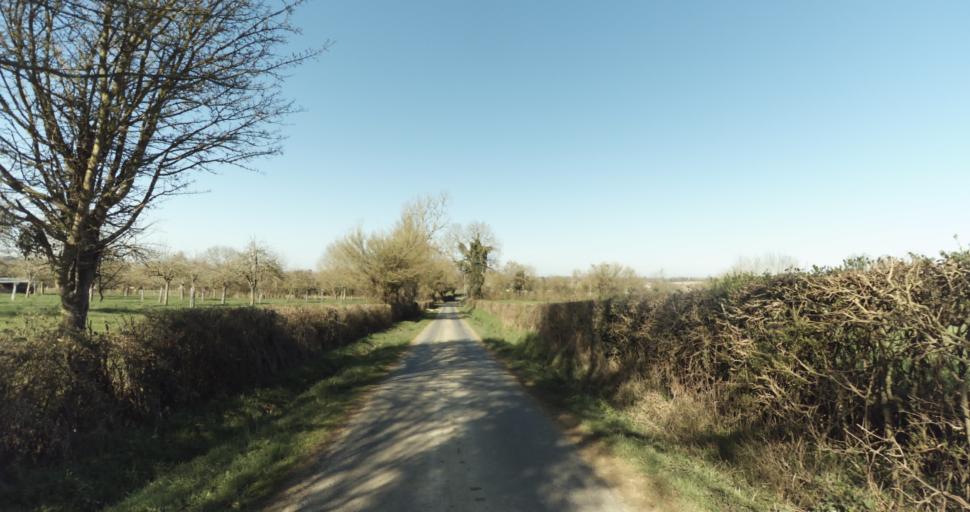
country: FR
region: Lower Normandy
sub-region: Departement du Calvados
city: Saint-Pierre-sur-Dives
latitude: 48.9655
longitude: 0.0287
